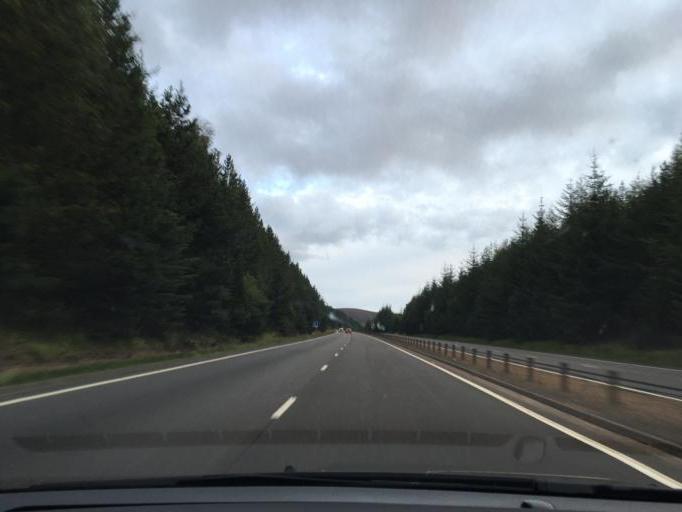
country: GB
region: Scotland
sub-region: Highland
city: Inverness
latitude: 57.3988
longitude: -4.1292
